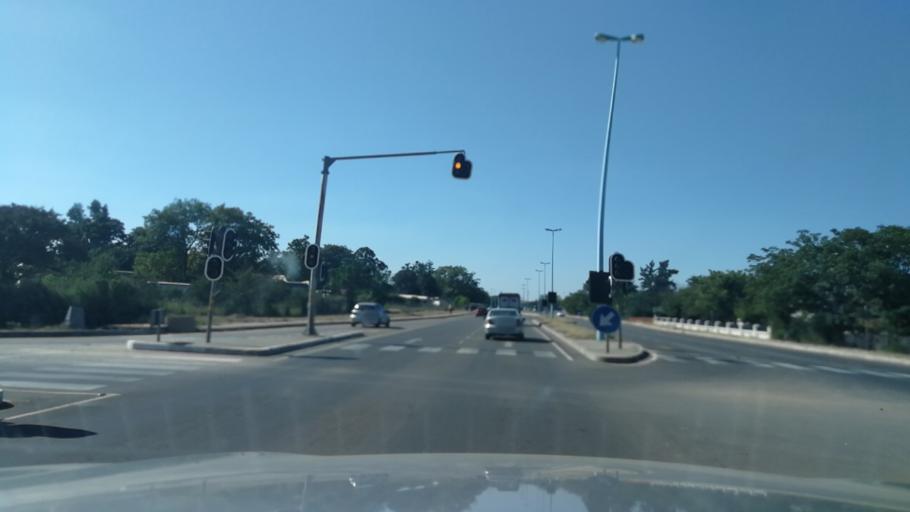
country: BW
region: South East
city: Gaborone
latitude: -24.6757
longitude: 25.9213
